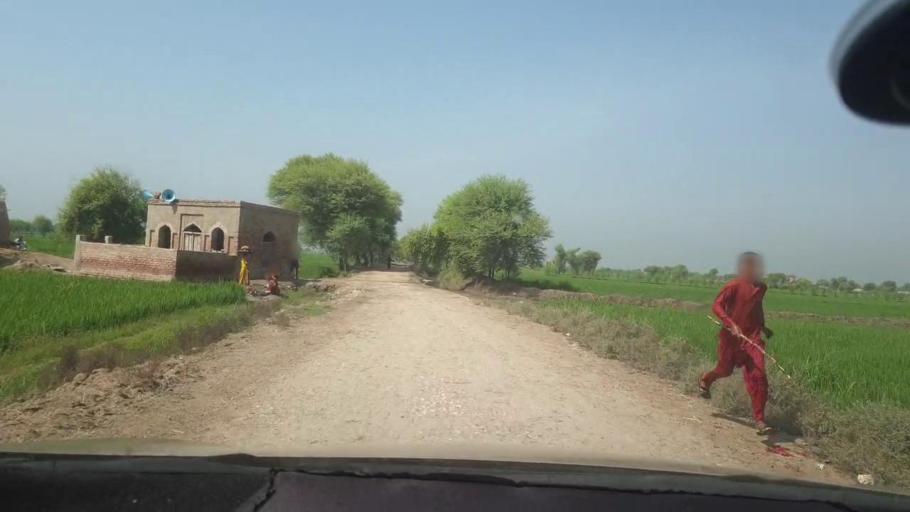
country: PK
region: Sindh
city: Kambar
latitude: 27.6962
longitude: 67.9170
